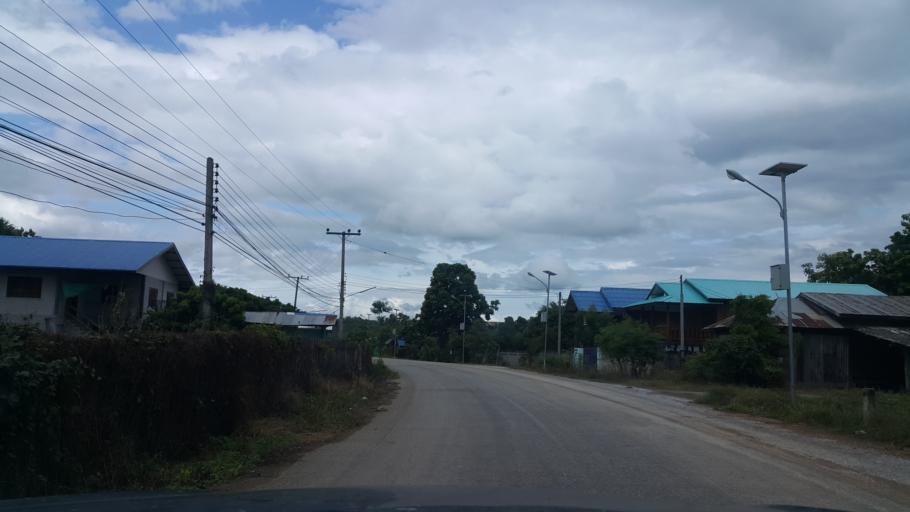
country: TH
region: Sukhothai
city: Thung Saliam
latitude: 17.3130
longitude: 99.5738
